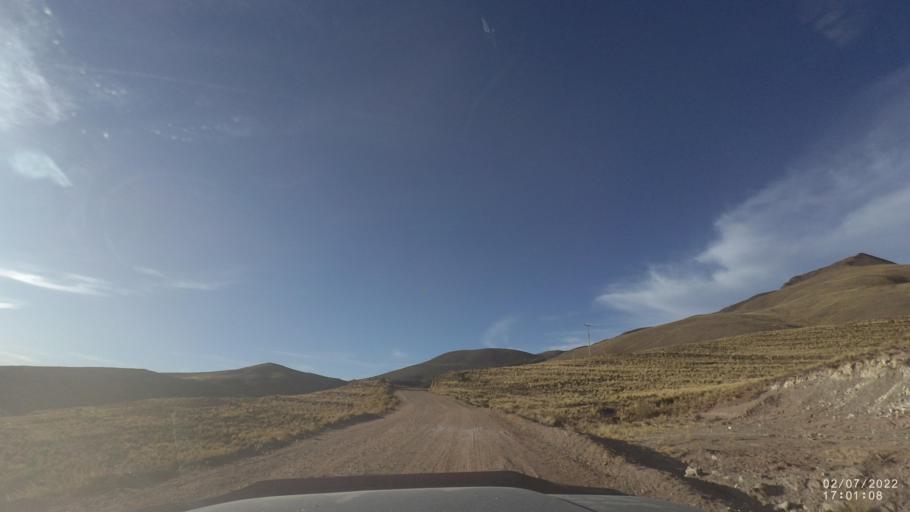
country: BO
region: Cochabamba
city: Irpa Irpa
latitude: -17.9335
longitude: -66.5557
